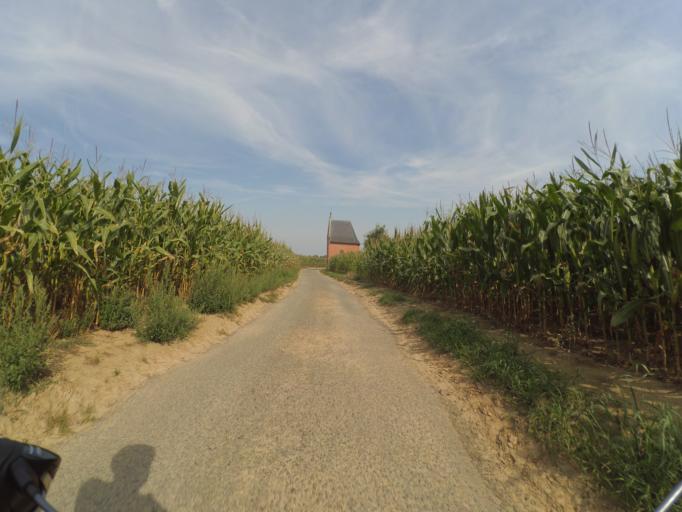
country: BE
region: Wallonia
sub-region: Province du Hainaut
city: Ellezelles
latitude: 50.7151
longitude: 3.6966
